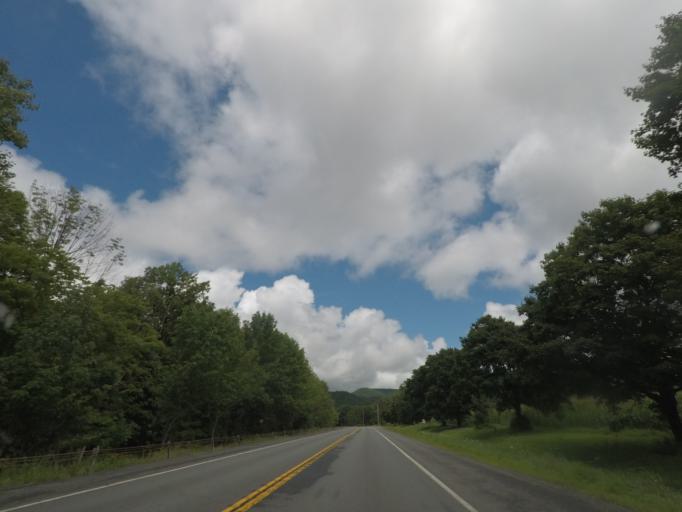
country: US
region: Massachusetts
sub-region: Berkshire County
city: Lanesborough
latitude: 42.6307
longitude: -73.3600
